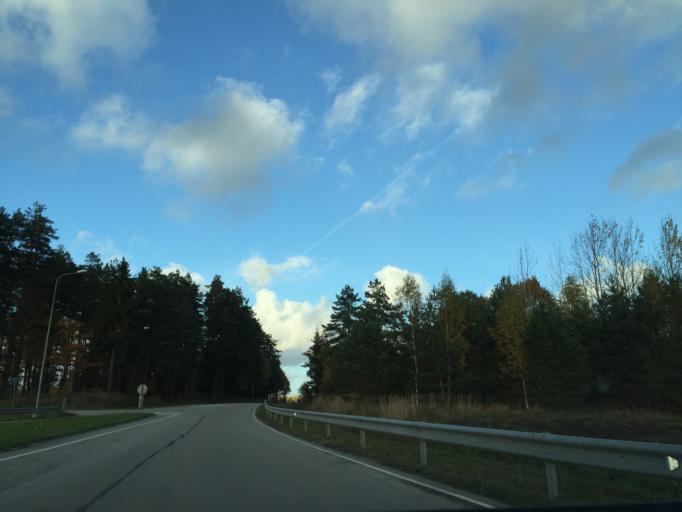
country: LV
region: Ogre
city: Jumprava
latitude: 56.7832
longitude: 25.0198
